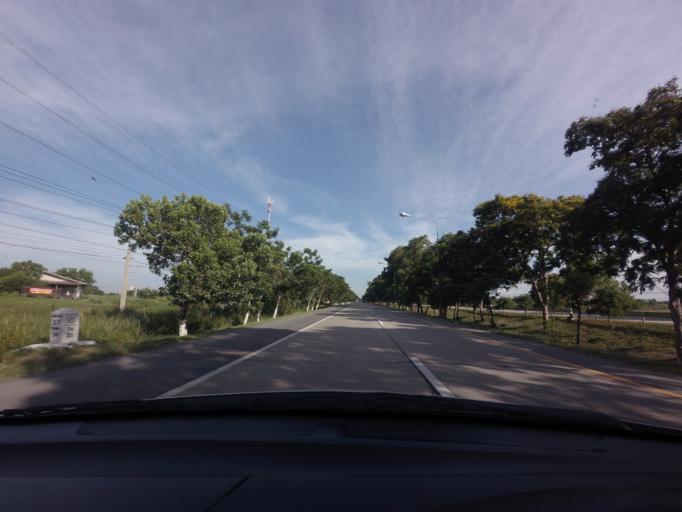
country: TH
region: Suphan Buri
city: Bang Pla Ma
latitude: 14.3623
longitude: 100.1840
